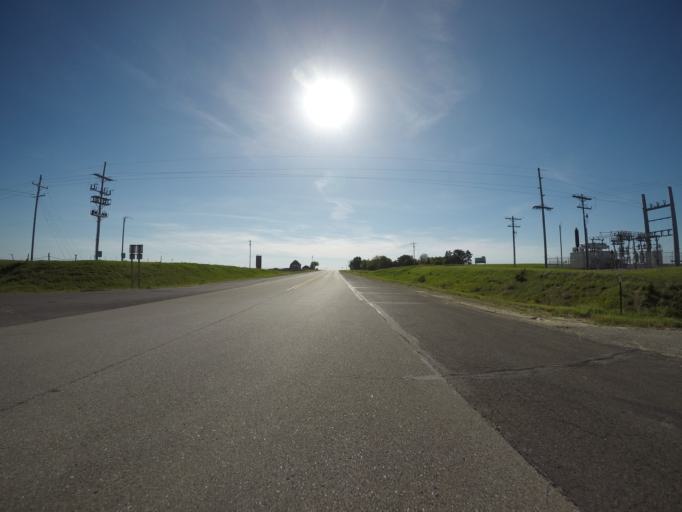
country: US
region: Kansas
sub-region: Clay County
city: Clay Center
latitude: 39.3647
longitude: -96.9236
